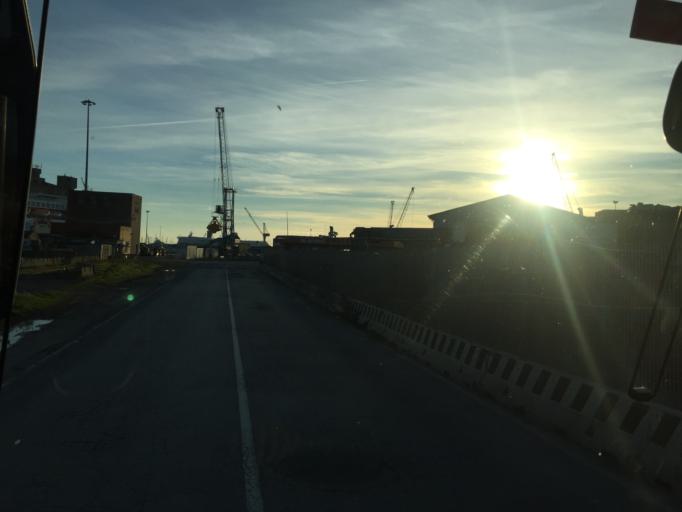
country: IT
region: Tuscany
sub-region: Provincia di Livorno
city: Livorno
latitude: 43.5557
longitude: 10.3001
